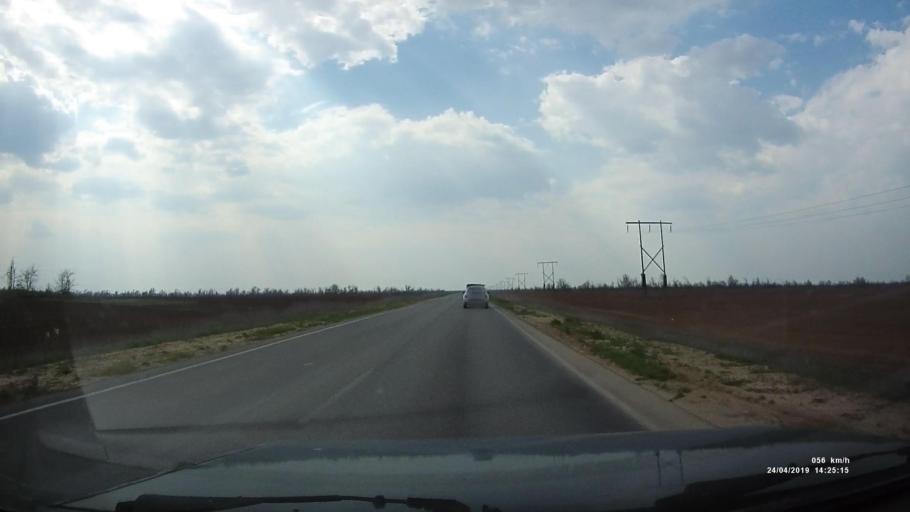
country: RU
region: Kalmykiya
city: Arshan'
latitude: 46.3302
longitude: 44.0838
